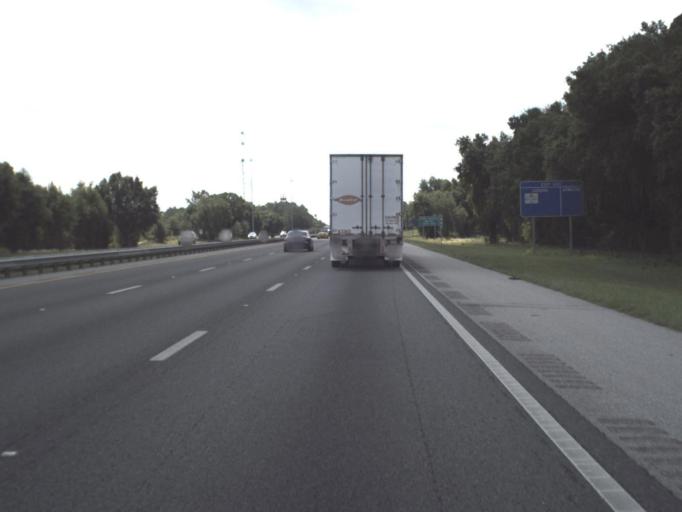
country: US
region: Florida
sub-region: Suwannee County
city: Wellborn
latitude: 30.3231
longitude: -82.8135
